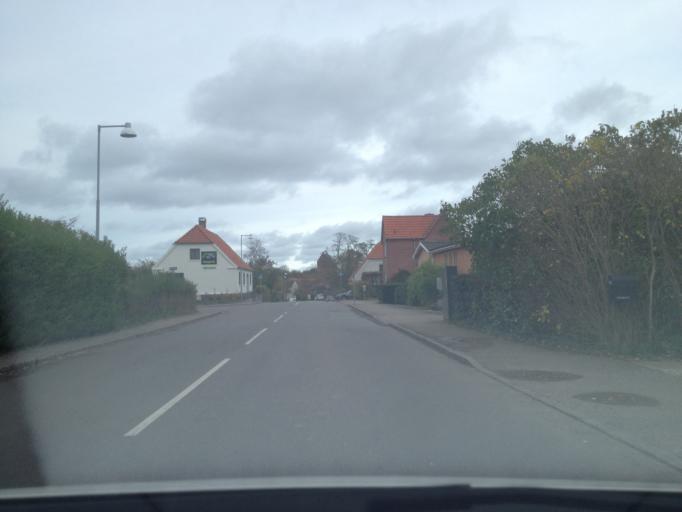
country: DK
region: Zealand
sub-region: Odsherred Kommune
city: Hojby
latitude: 55.9105
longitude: 11.5927
